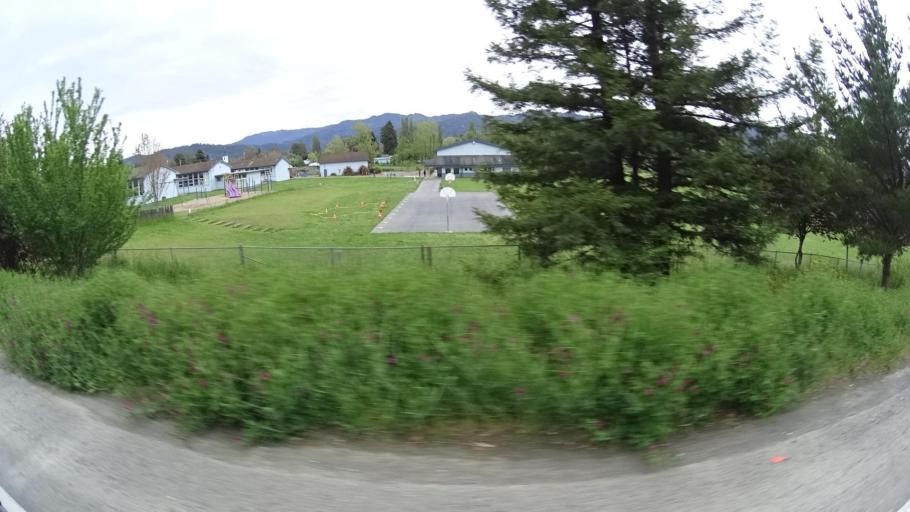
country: US
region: California
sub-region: Humboldt County
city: Blue Lake
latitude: 40.8859
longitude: -123.9924
